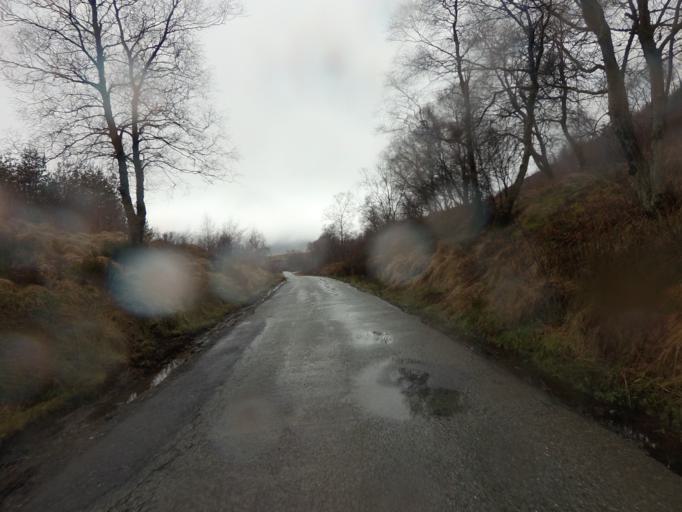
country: GB
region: Scotland
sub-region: West Dunbartonshire
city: Balloch
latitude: 56.2426
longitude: -4.5713
